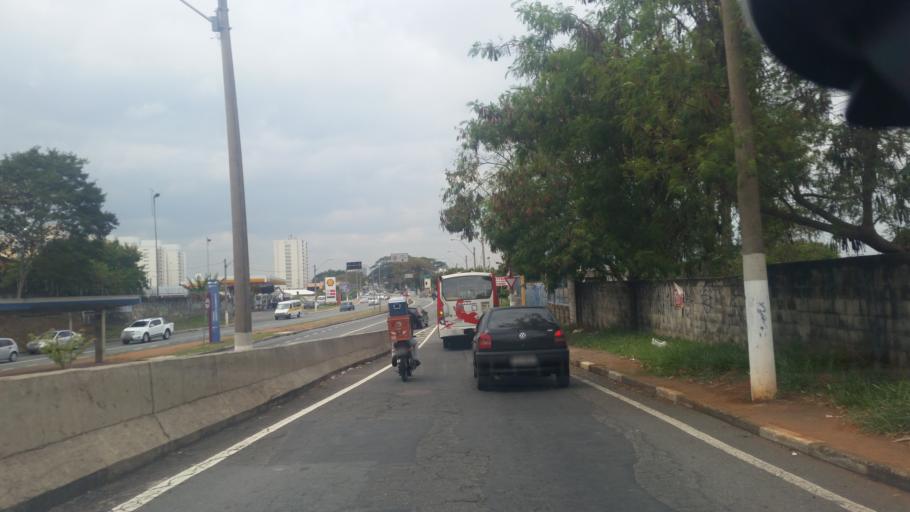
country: BR
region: Sao Paulo
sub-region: Campinas
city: Campinas
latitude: -22.9019
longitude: -47.0818
